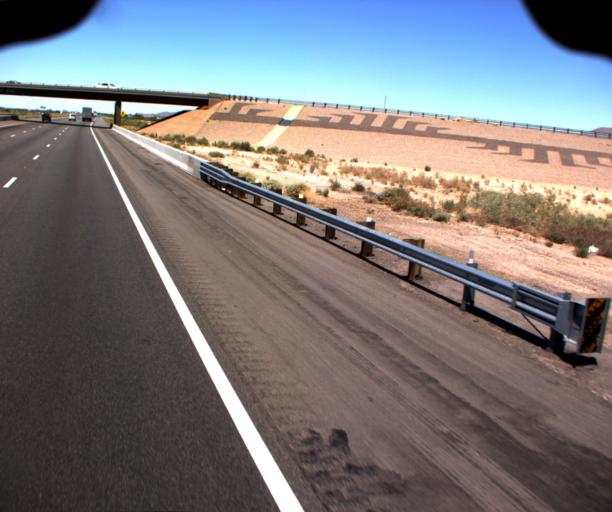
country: US
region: Arizona
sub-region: Pinal County
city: Casa Grande
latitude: 32.9373
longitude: -111.6999
